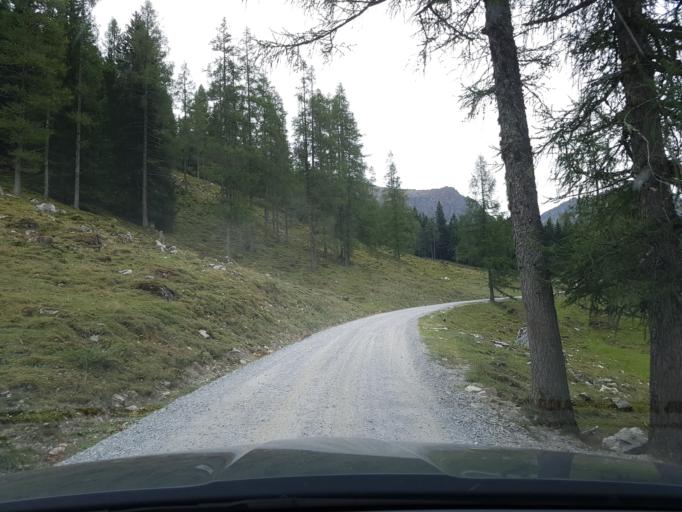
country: AT
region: Salzburg
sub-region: Politischer Bezirk Sankt Johann im Pongau
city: Forstau
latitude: 47.3043
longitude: 13.5822
